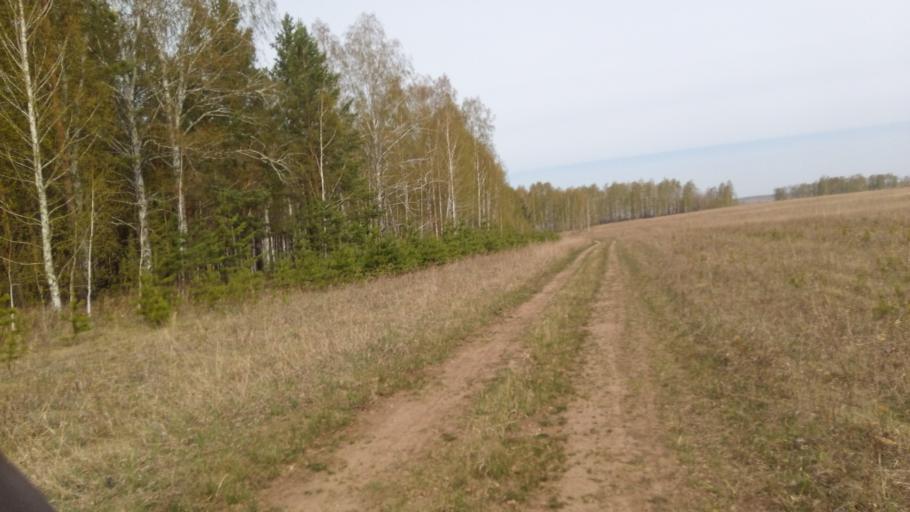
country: RU
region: Chelyabinsk
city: Timiryazevskiy
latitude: 55.0198
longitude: 60.8595
